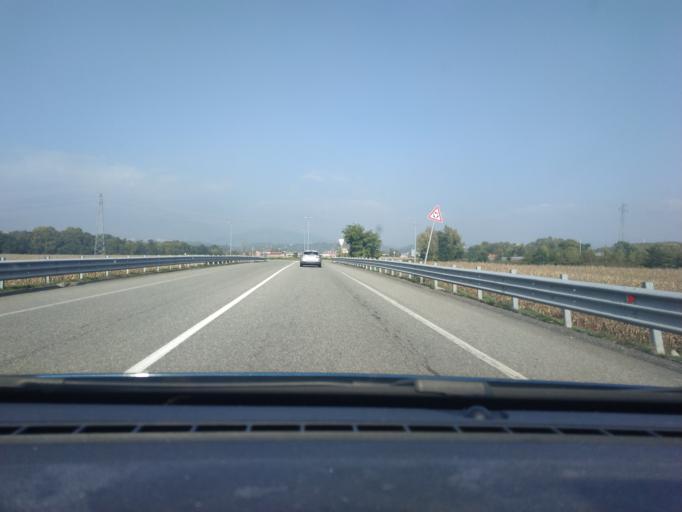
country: IT
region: Piedmont
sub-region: Provincia di Biella
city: Ponderano
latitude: 45.5381
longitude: 8.0390
